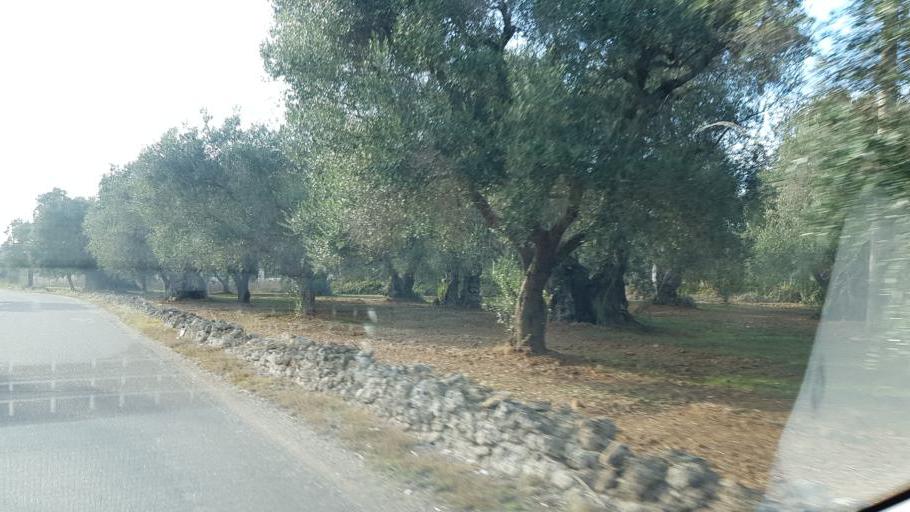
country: IT
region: Apulia
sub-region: Provincia di Brindisi
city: Oria
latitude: 40.5097
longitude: 17.6675
